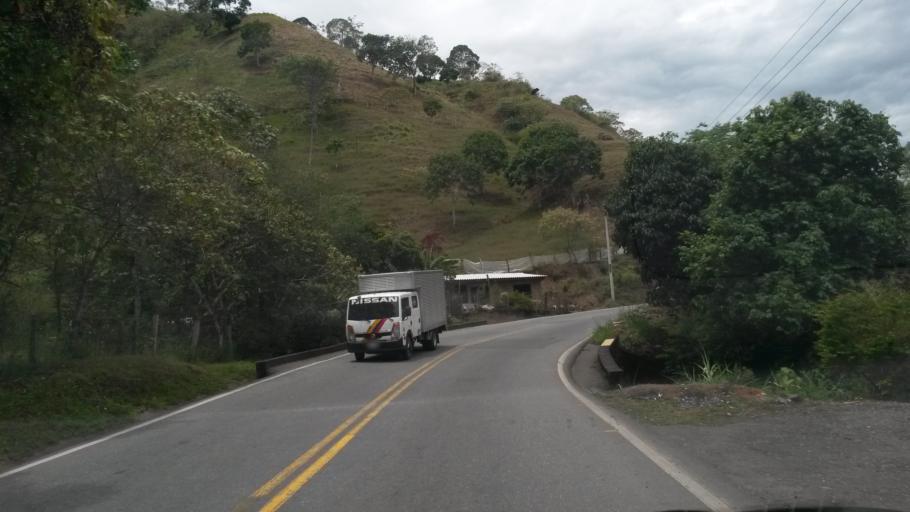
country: CO
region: Cauca
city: Rosas
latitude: 2.2539
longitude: -76.7615
